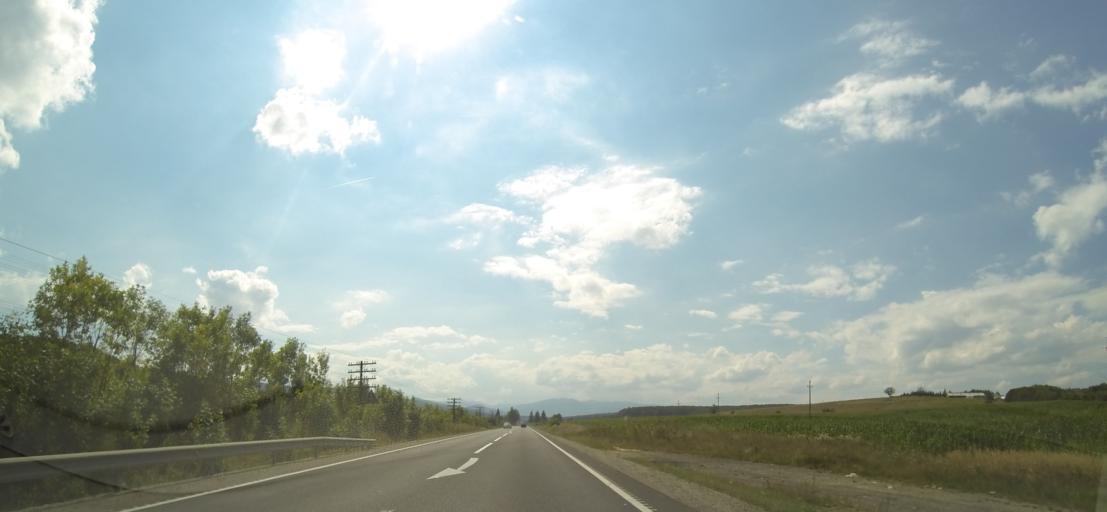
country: RO
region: Brasov
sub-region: Comuna Sinca Noua
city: Sinca Noua
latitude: 45.7554
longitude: 25.3147
